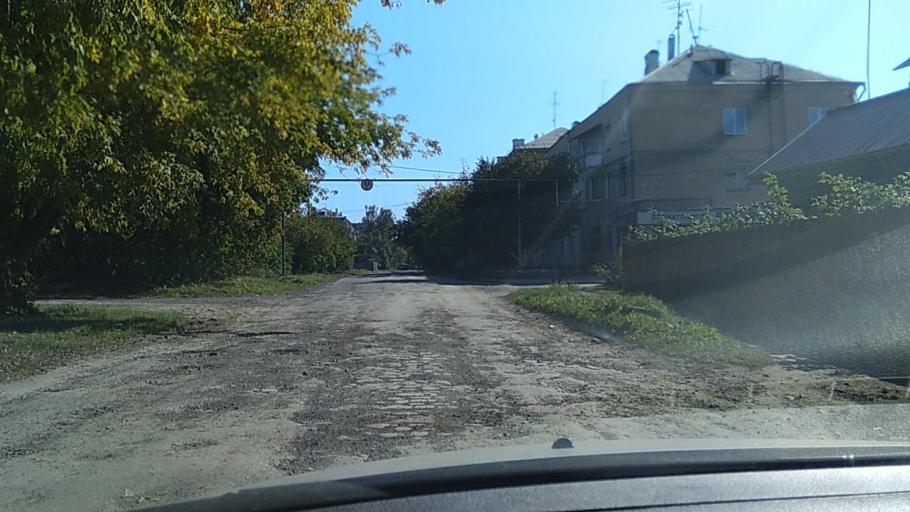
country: RU
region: Sverdlovsk
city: Yekaterinburg
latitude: 56.8890
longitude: 60.5635
